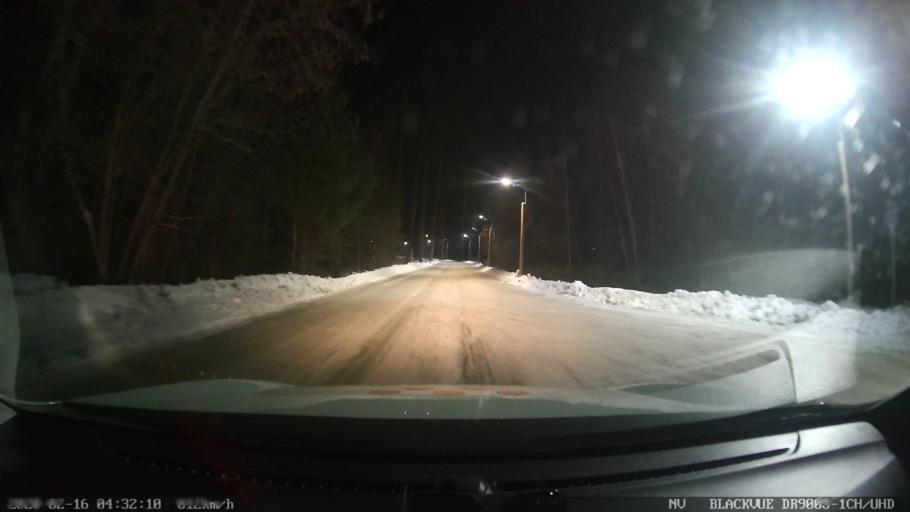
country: RU
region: Tatarstan
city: Staroye Arakchino
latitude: 55.8354
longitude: 48.9652
